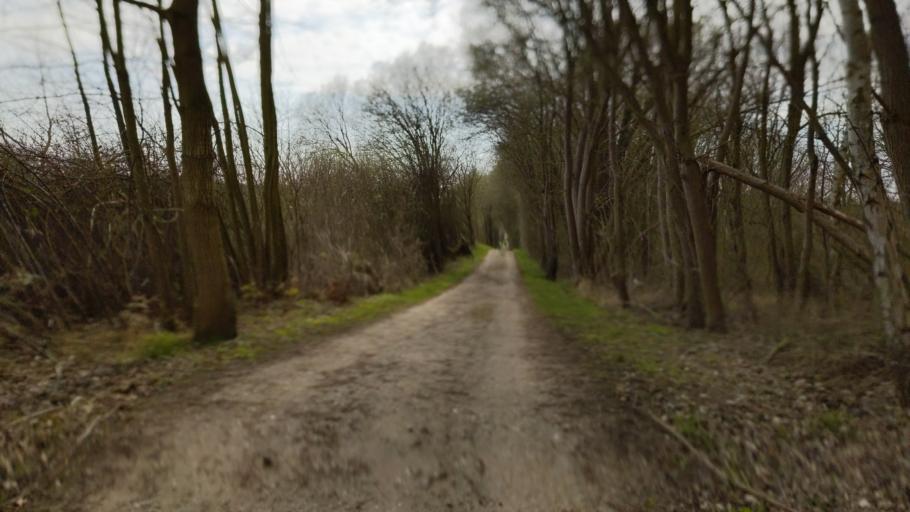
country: DE
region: Mecklenburg-Vorpommern
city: Dassow
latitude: 53.9672
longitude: 10.9411
